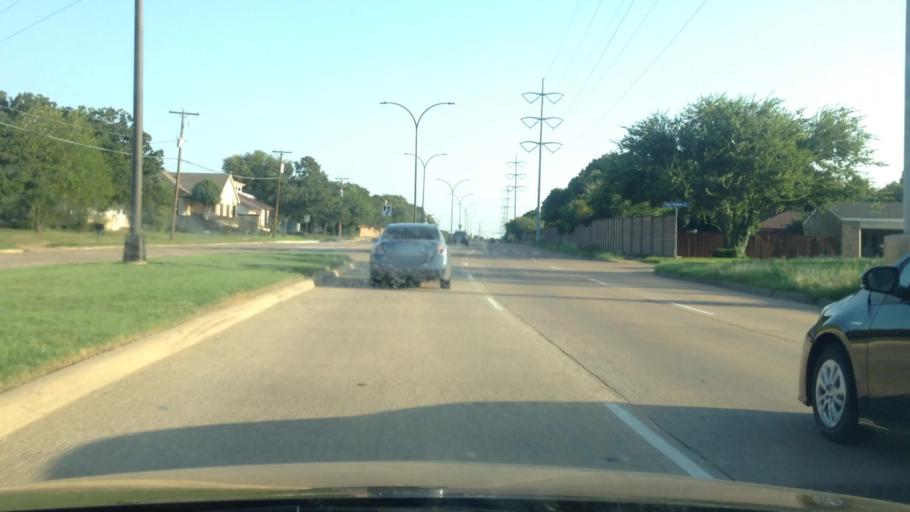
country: US
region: Texas
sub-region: Tarrant County
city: Dalworthington Gardens
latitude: 32.7014
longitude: -97.1904
